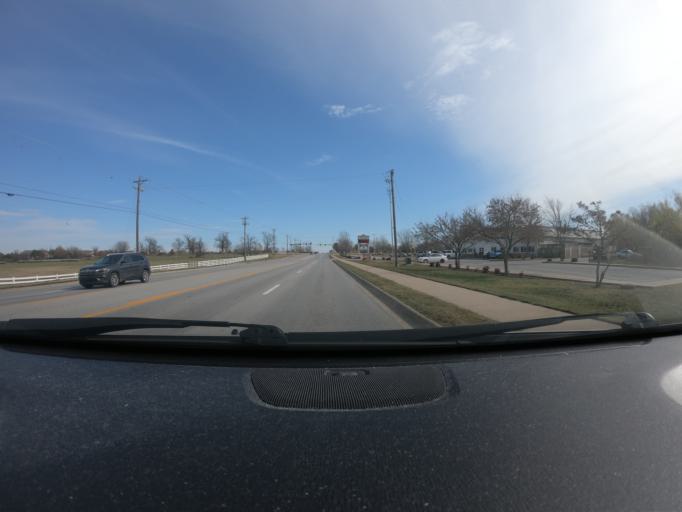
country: US
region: Arkansas
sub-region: Benton County
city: Bentonville
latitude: 36.3358
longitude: -94.2307
